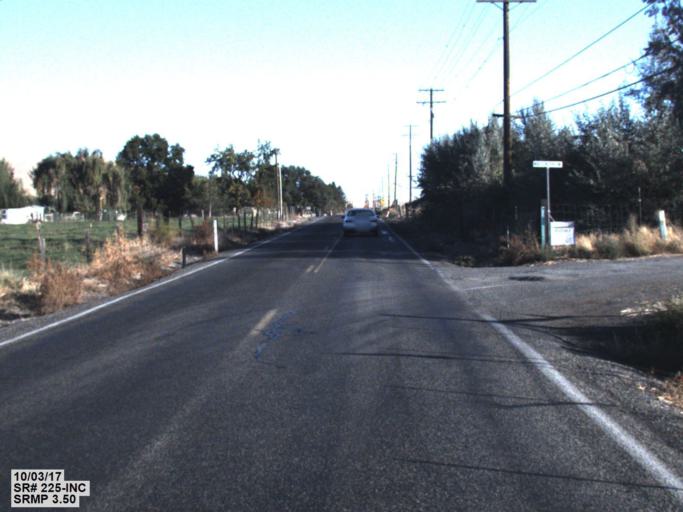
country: US
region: Washington
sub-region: Benton County
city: Benton City
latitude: 46.2939
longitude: -119.4938
